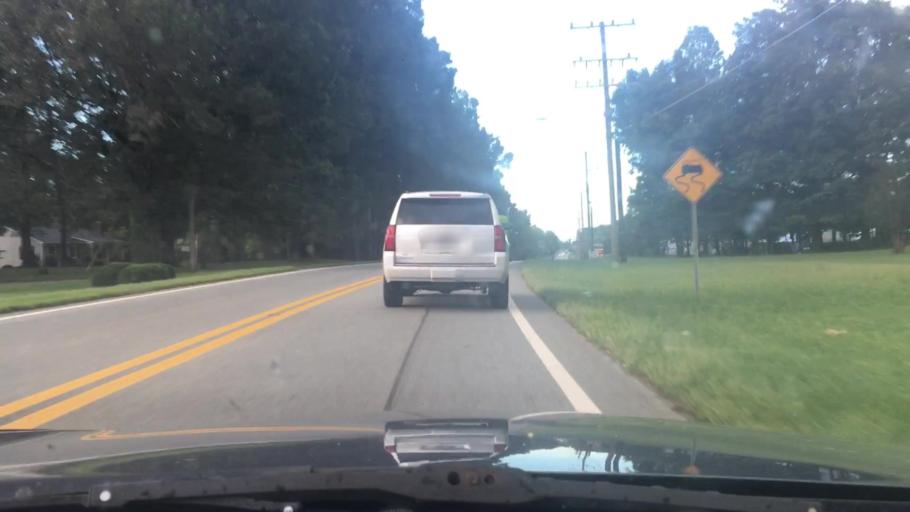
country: US
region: North Carolina
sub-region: Alamance County
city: Green Level
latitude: 36.1306
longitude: -79.3452
